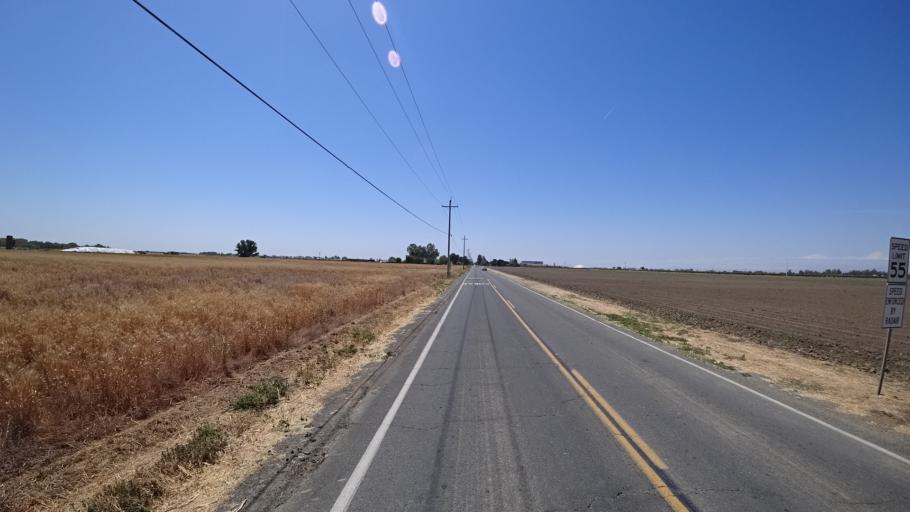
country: US
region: California
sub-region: Kings County
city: Lemoore
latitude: 36.2535
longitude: -119.7629
